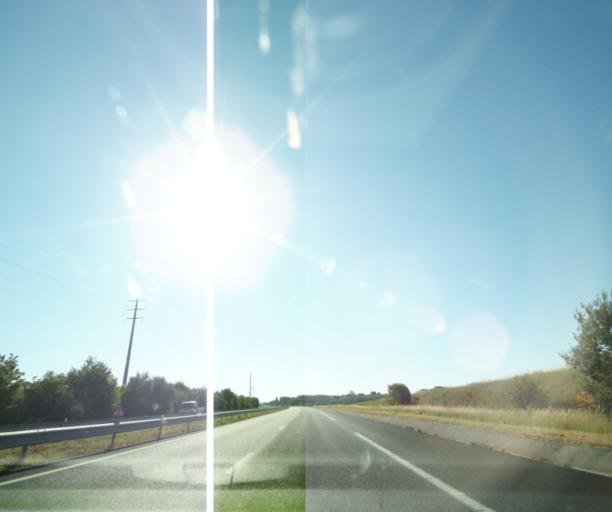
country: FR
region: Champagne-Ardenne
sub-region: Departement de l'Aube
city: Saint-Pouange
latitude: 48.2356
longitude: 4.0228
